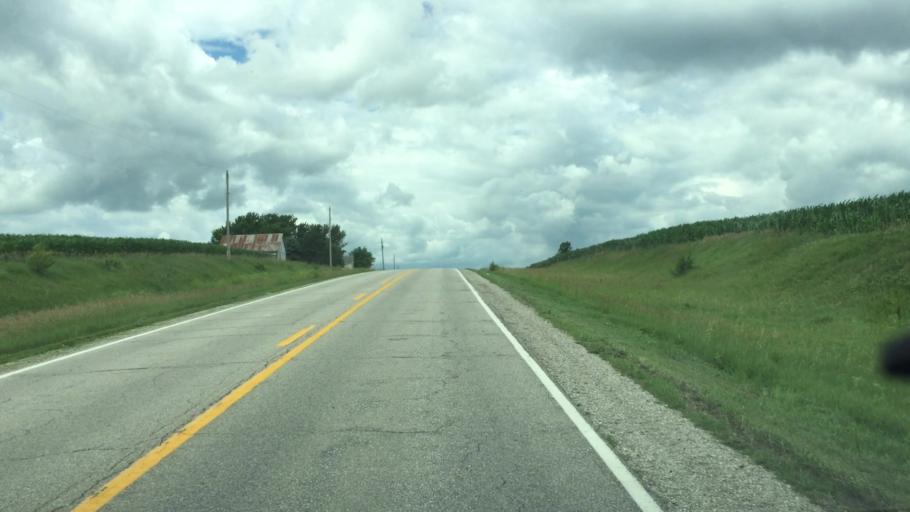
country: US
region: Iowa
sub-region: Jasper County
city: Monroe
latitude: 41.5735
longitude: -93.0694
